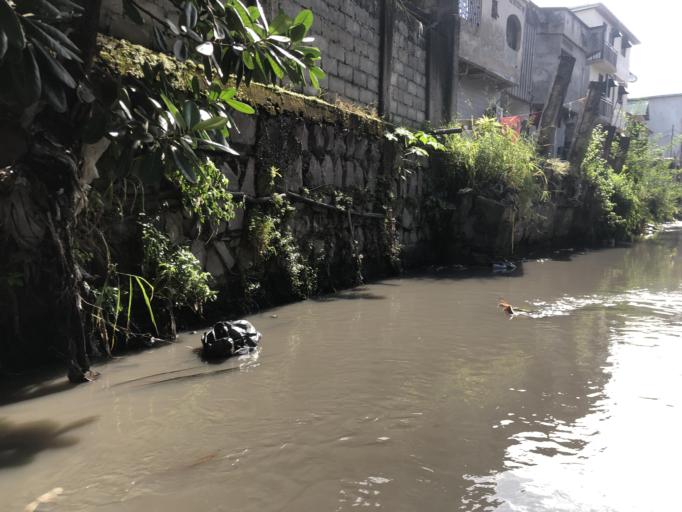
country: CD
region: Kinshasa
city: Kinshasa
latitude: -4.3193
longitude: 15.2705
